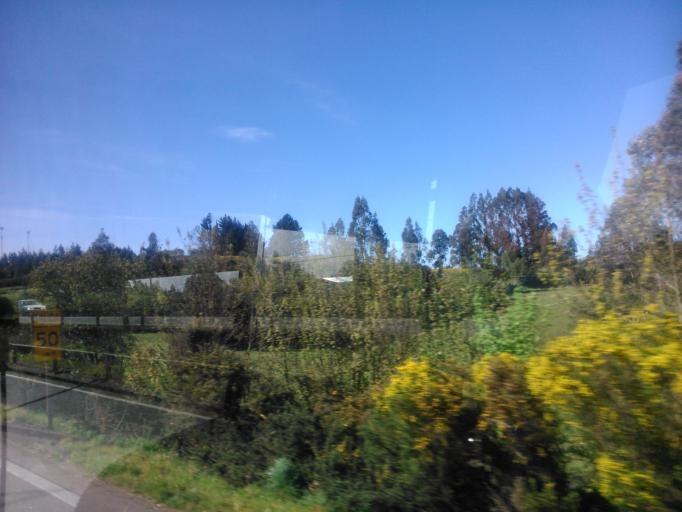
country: CL
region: Araucania
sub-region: Provincia de Cautin
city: Temuco
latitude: -38.8093
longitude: -72.6261
